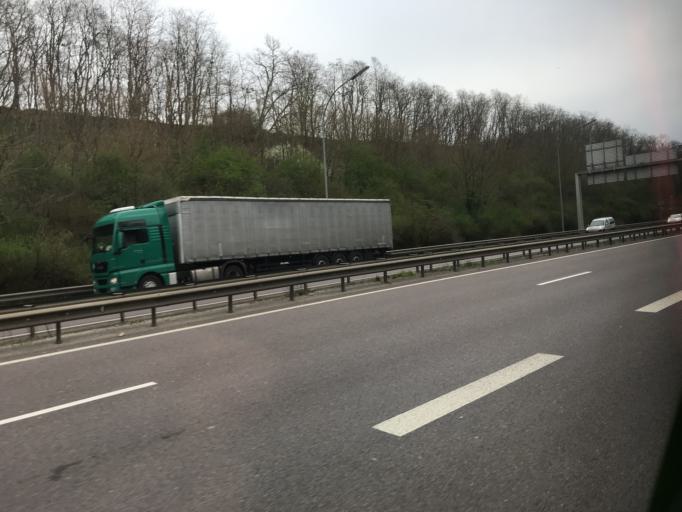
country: LU
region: Luxembourg
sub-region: Canton d'Esch-sur-Alzette
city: Leudelange
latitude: 49.5814
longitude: 6.0876
